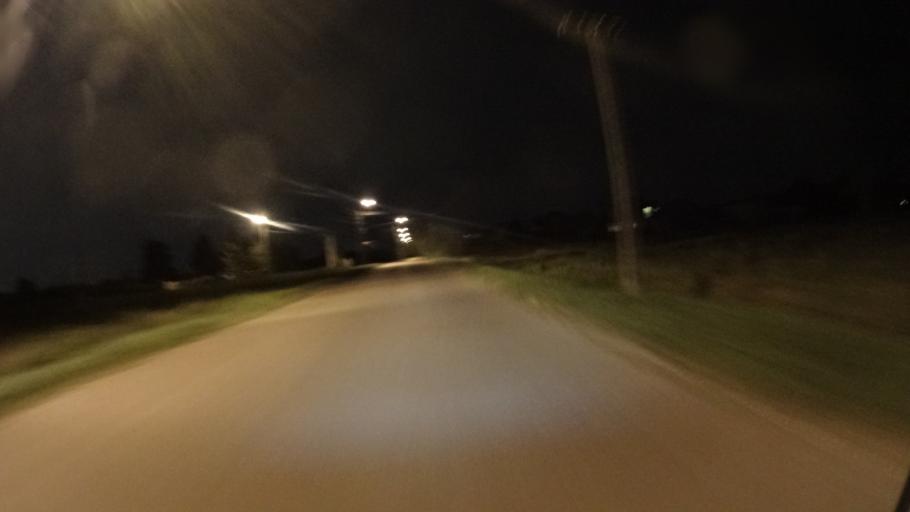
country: PL
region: Masovian Voivodeship
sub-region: Powiat warszawski zachodni
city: Ozarow Mazowiecki
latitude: 52.2467
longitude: 20.7870
